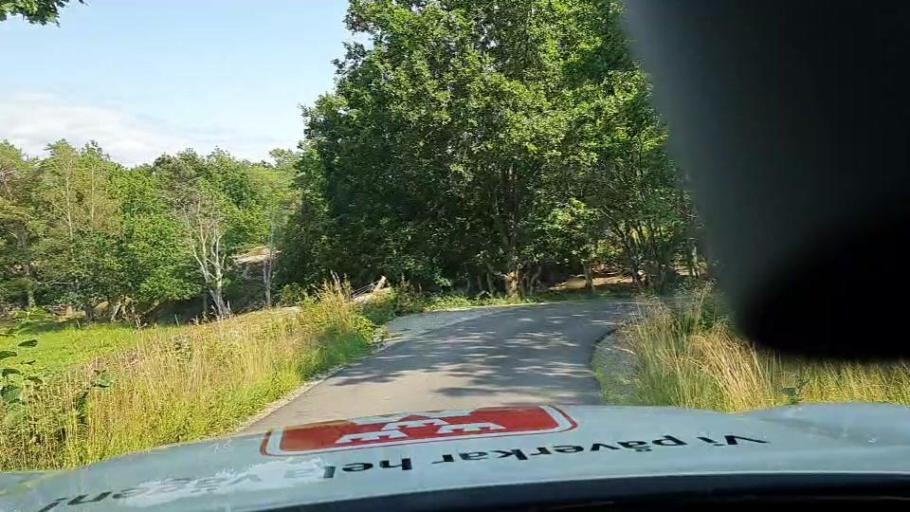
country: SE
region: Vaestra Goetaland
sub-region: Tjorns Kommun
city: Myggenas
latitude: 58.1153
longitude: 11.6545
